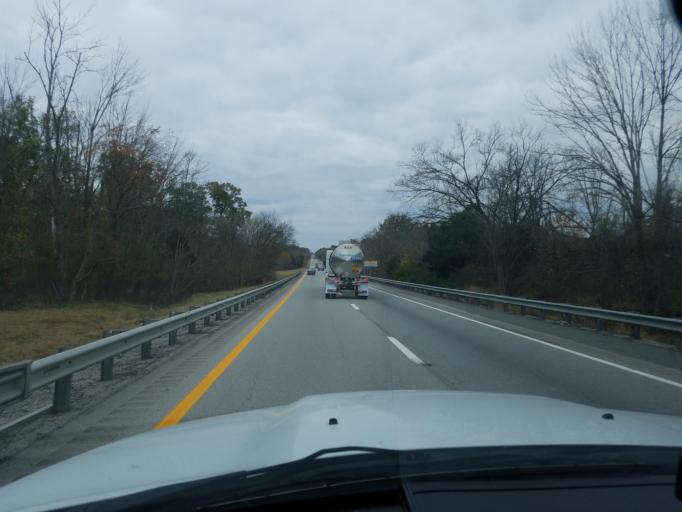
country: US
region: Kentucky
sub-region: Oldham County
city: La Grange
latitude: 38.4265
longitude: -85.3264
